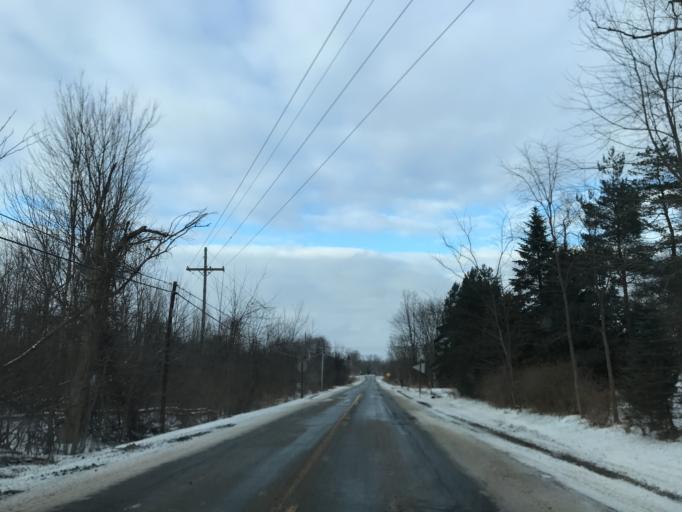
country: US
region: Michigan
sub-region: Oakland County
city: South Lyon
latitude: 42.4160
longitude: -83.5895
